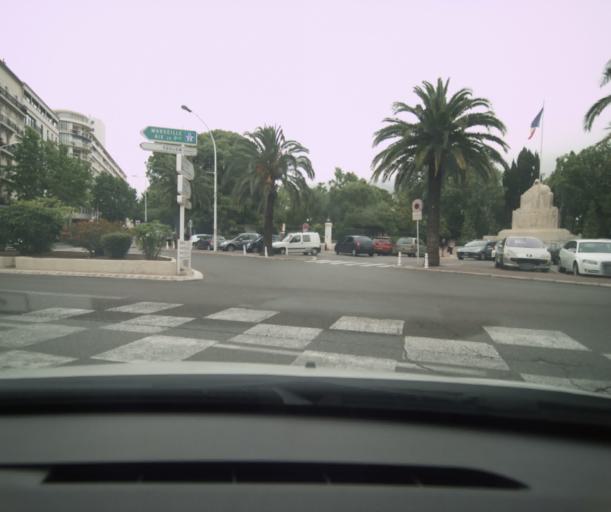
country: FR
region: Provence-Alpes-Cote d'Azur
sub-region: Departement du Var
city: Toulon
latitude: 43.1262
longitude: 5.9258
